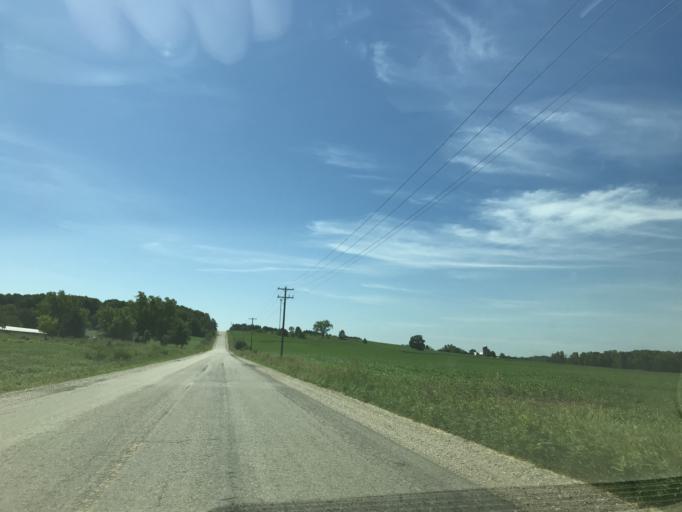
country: US
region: Michigan
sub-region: Missaukee County
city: Lake City
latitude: 44.3023
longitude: -85.0746
